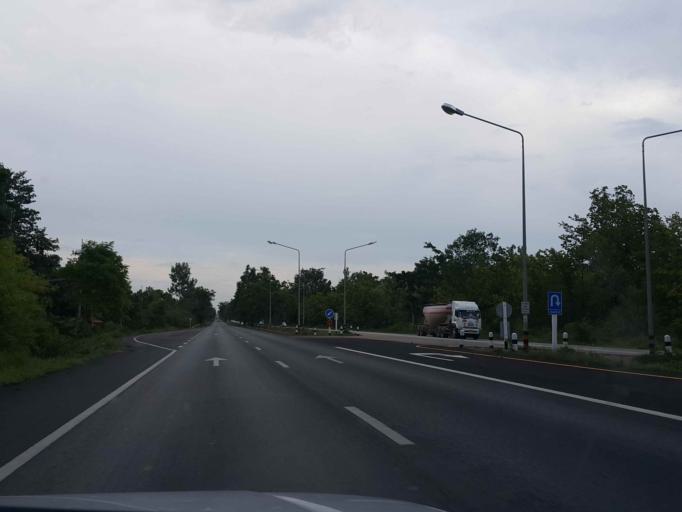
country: TH
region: Lampang
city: Ko Kha
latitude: 18.0703
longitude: 99.3914
